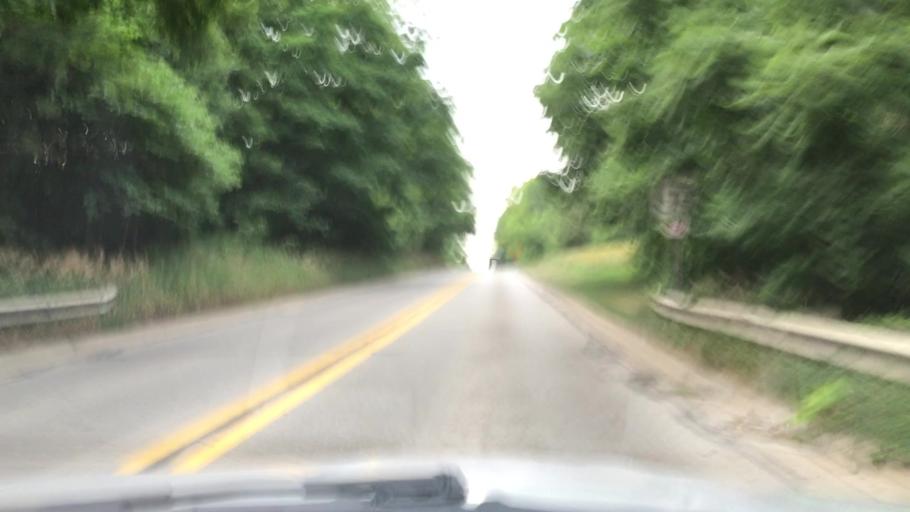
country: US
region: Michigan
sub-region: Wayne County
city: Northville
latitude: 42.4313
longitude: -83.5121
